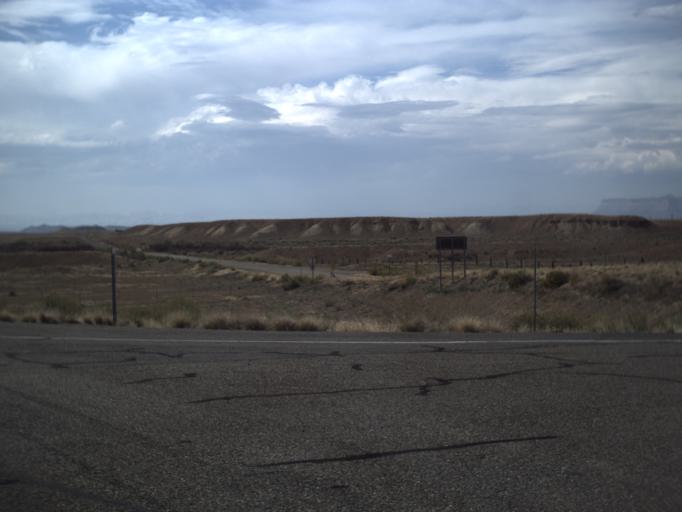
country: US
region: Utah
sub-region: Grand County
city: Moab
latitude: 38.9217
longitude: -109.9356
